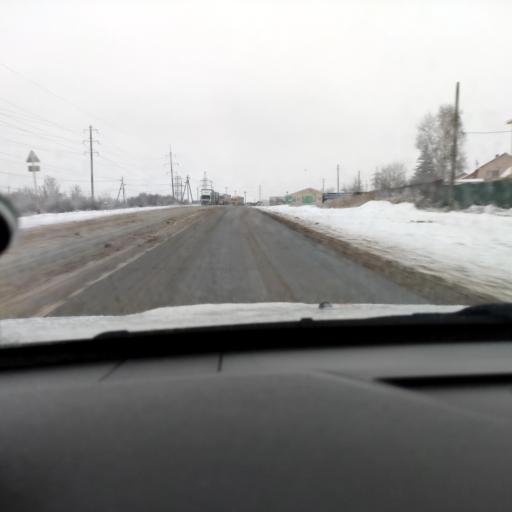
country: RU
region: Samara
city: Smyshlyayevka
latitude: 53.2469
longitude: 50.4750
